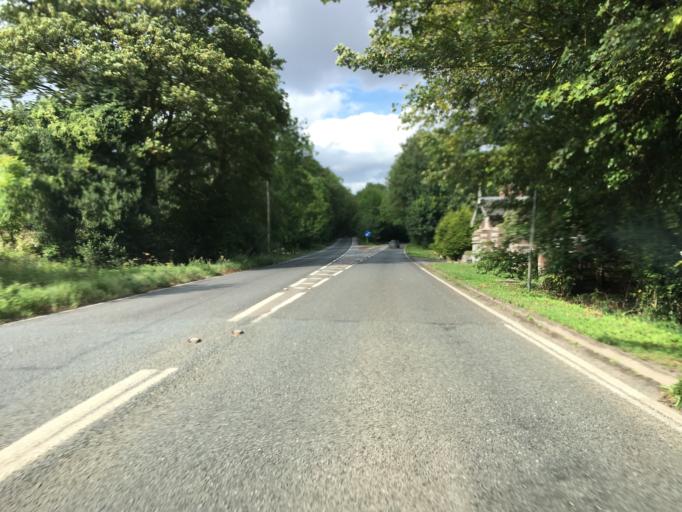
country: GB
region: England
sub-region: Hampshire
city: Overton
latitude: 51.1630
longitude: -1.2335
